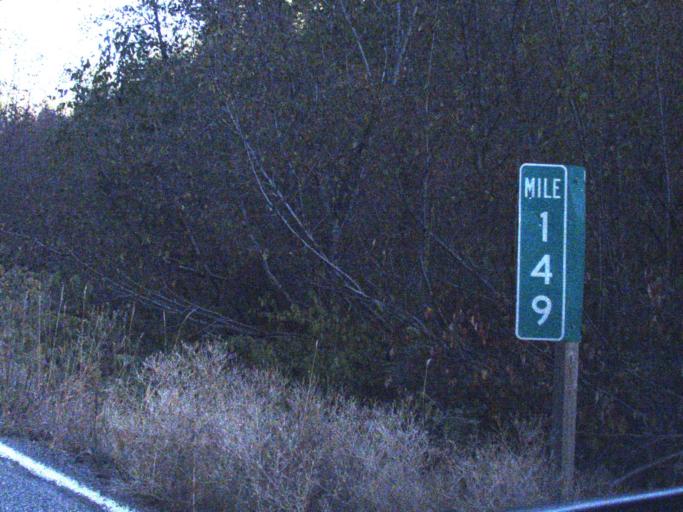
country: US
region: Washington
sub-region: Ferry County
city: Republic
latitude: 48.4913
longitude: -118.7394
